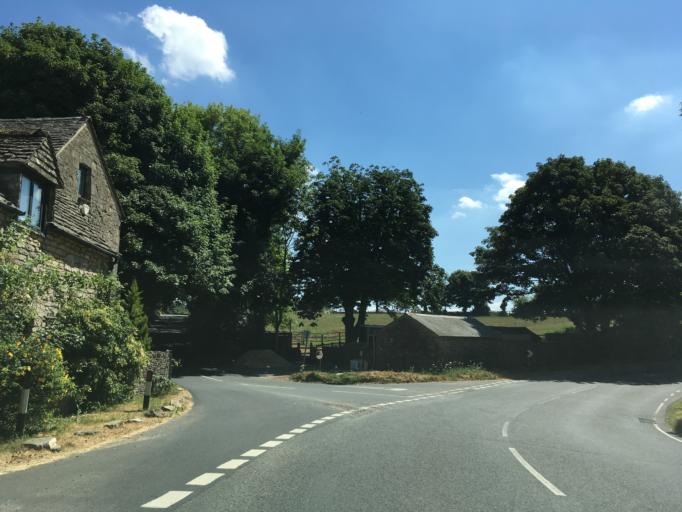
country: GB
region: England
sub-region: Gloucestershire
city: Chalford
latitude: 51.7475
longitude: -2.1381
